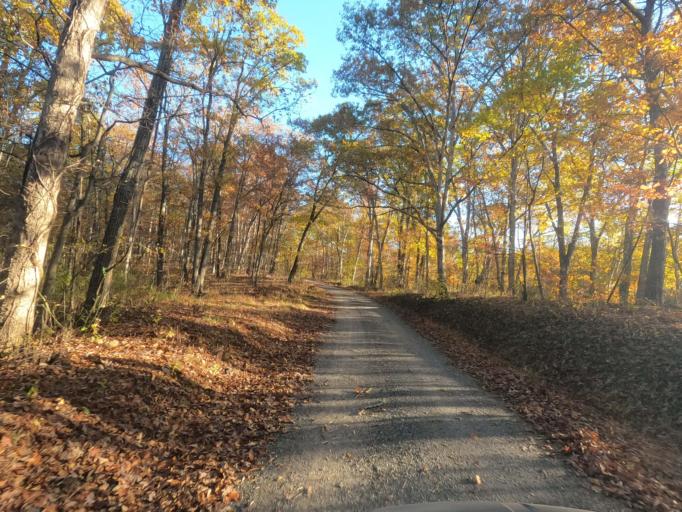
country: US
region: West Virginia
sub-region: Mineral County
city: Fort Ashby
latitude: 39.5291
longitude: -78.5385
